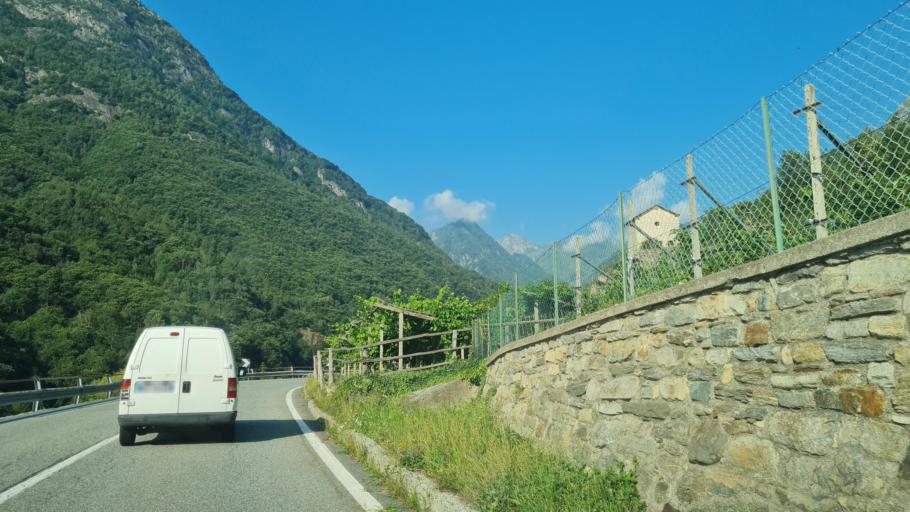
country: IT
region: Aosta Valley
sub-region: Valle d'Aosta
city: Hone
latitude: 45.6126
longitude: 7.7297
